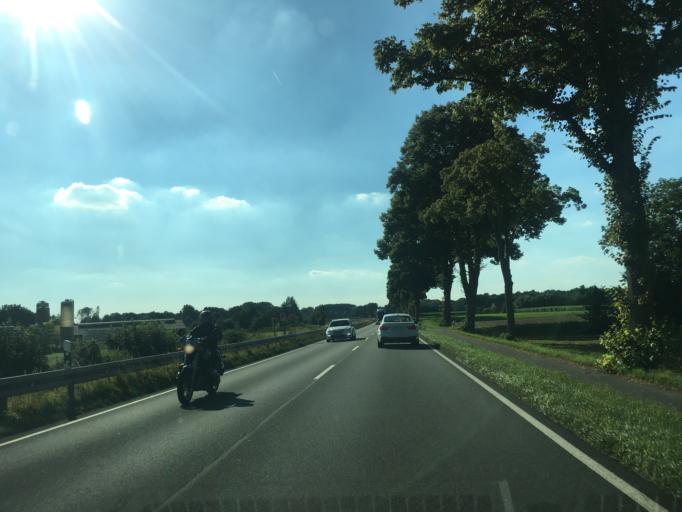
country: DE
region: North Rhine-Westphalia
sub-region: Regierungsbezirk Munster
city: Warendorf
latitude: 51.9593
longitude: 7.9146
